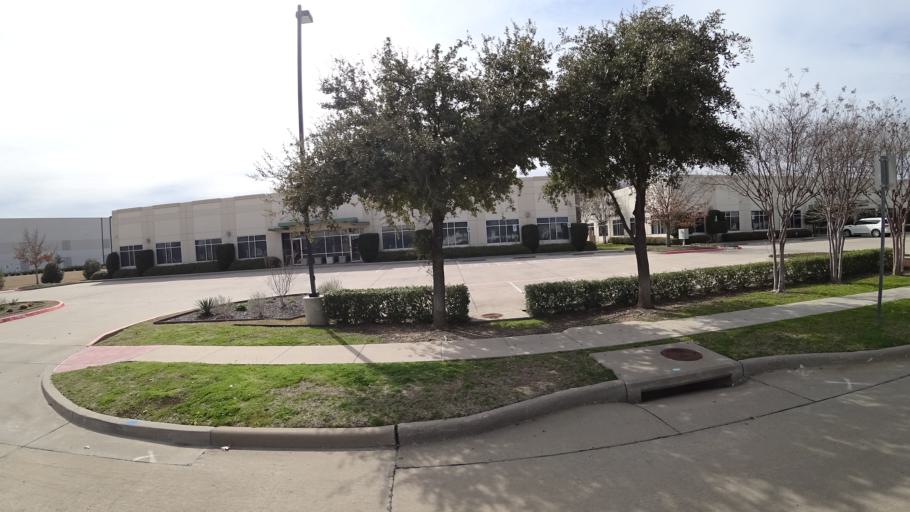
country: US
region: Texas
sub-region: Denton County
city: Lewisville
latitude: 33.0184
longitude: -96.9762
